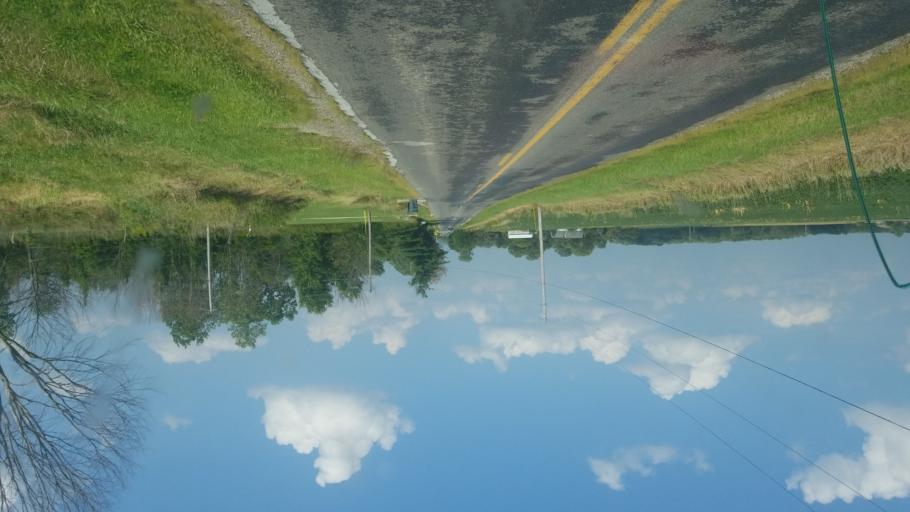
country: US
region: Ohio
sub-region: Wayne County
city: West Salem
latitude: 41.0685
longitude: -82.1306
